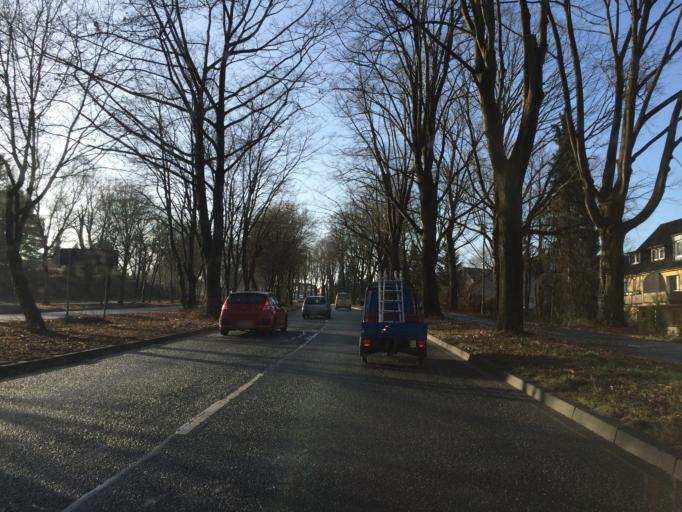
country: DE
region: North Rhine-Westphalia
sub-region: Regierungsbezirk Arnsberg
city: Bochum
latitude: 51.4510
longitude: 7.2253
